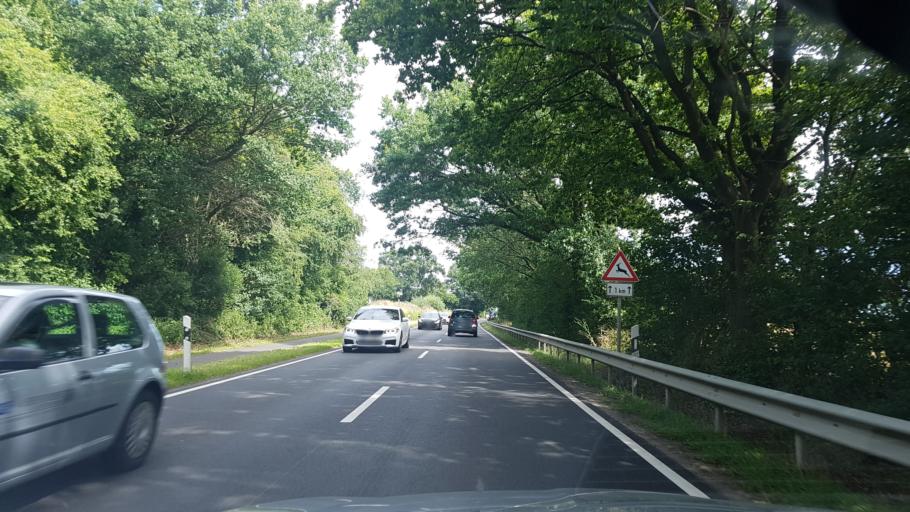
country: DE
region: Schleswig-Holstein
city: Bissee
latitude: 54.1629
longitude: 10.1338
